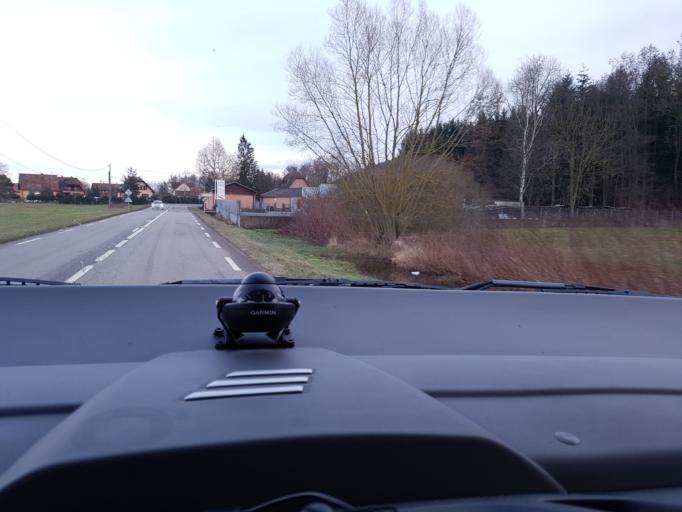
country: FR
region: Alsace
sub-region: Departement du Bas-Rhin
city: Chatenois
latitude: 48.2871
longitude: 7.3767
